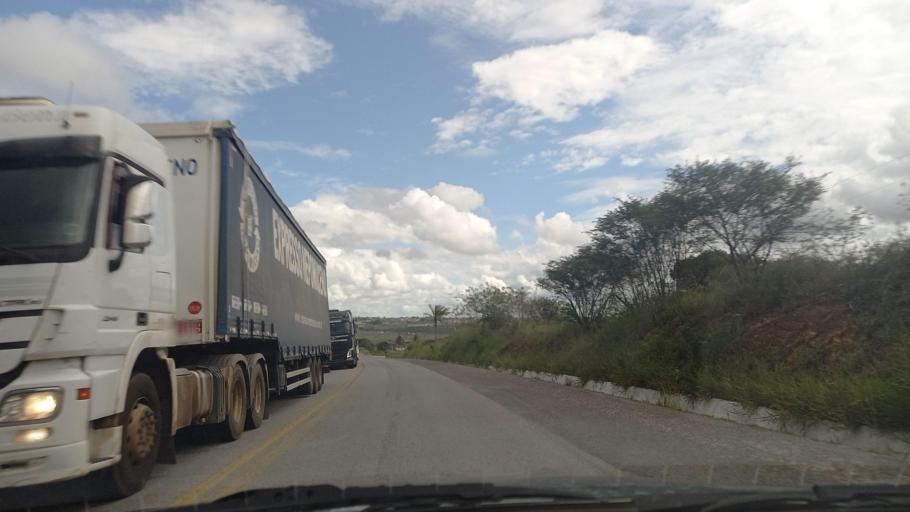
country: BR
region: Pernambuco
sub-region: Lajedo
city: Lajedo
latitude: -8.6848
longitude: -36.4083
